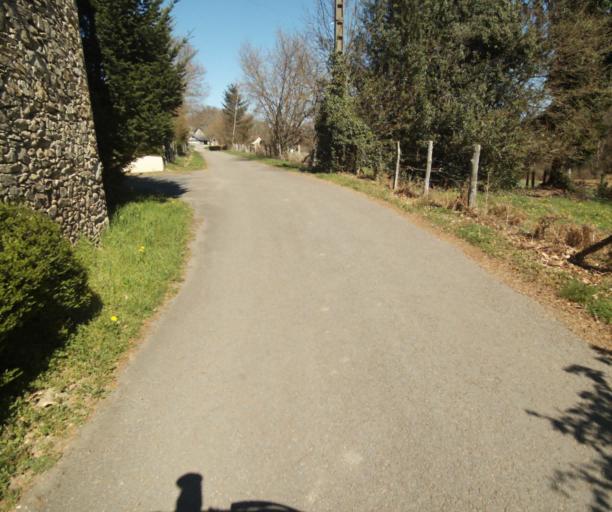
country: FR
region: Limousin
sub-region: Departement de la Correze
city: Saint-Mexant
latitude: 45.2770
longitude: 1.6653
